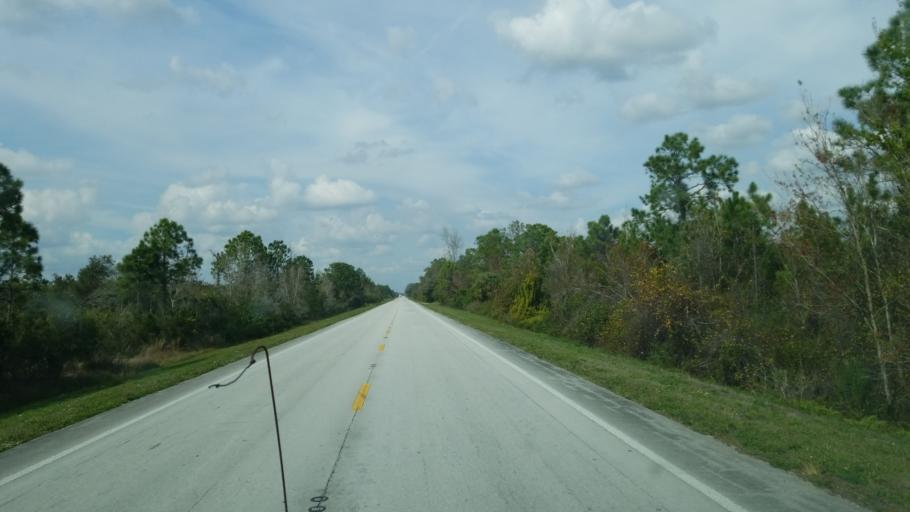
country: US
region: Florida
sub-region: Indian River County
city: Fellsmere
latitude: 27.6813
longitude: -80.8949
